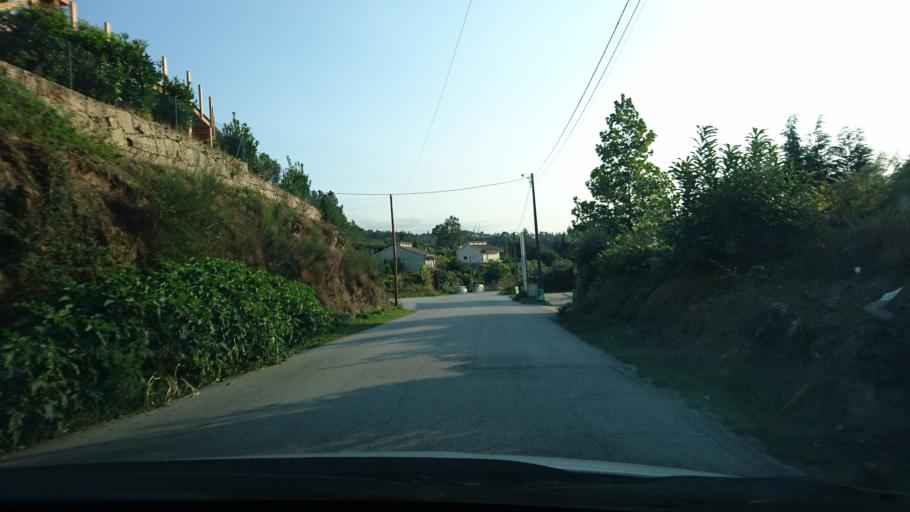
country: PT
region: Vila Real
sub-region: Mondim de Basto
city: Mondim de Basto
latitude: 41.4220
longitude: -7.9372
